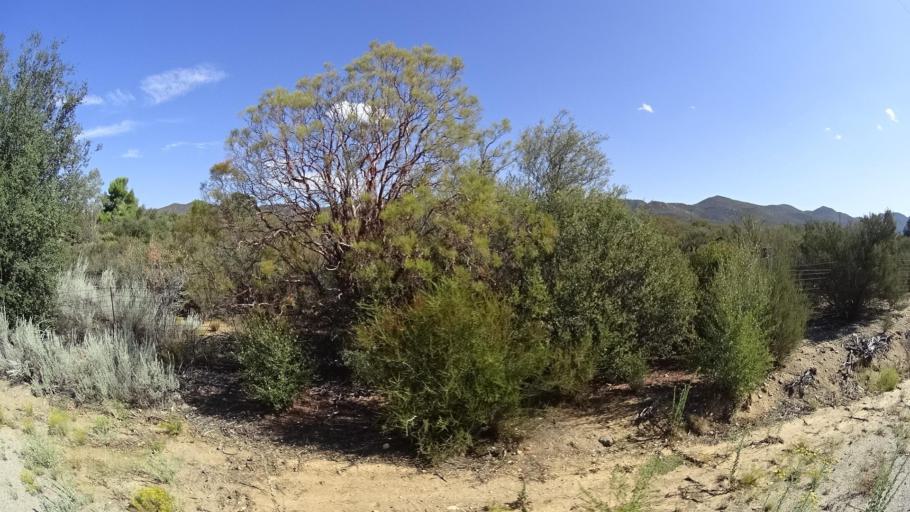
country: US
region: California
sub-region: Riverside County
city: Anza
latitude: 33.3857
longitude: -116.6625
